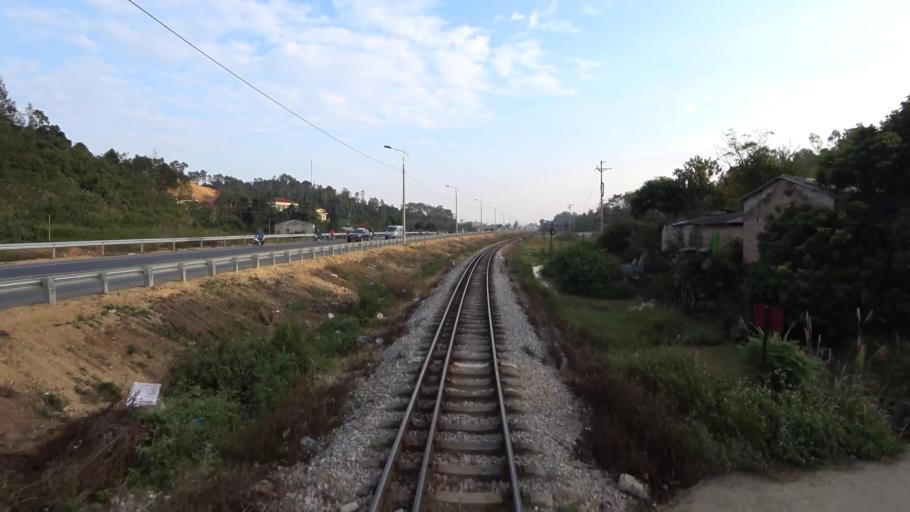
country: VN
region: Lang Son
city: Thi Tran Cao Loc
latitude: 21.8997
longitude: 106.7402
